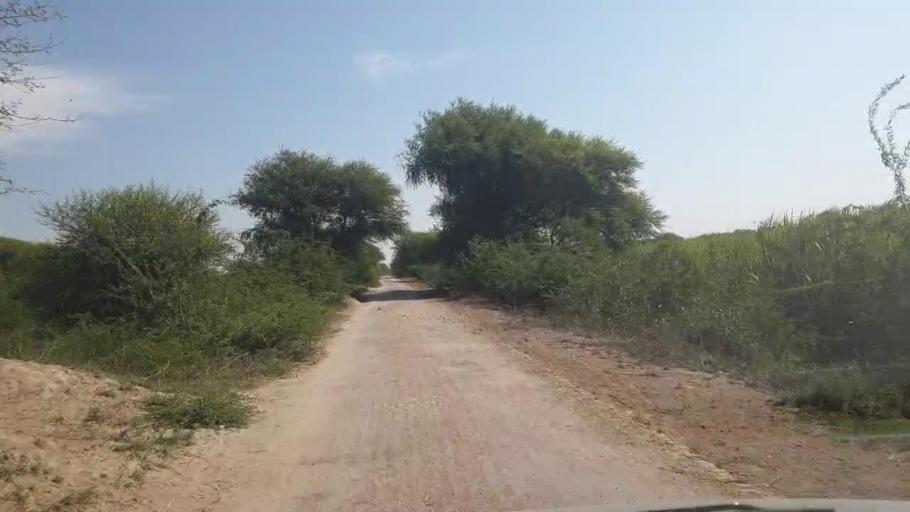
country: PK
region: Sindh
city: Digri
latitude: 24.9512
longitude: 69.1473
